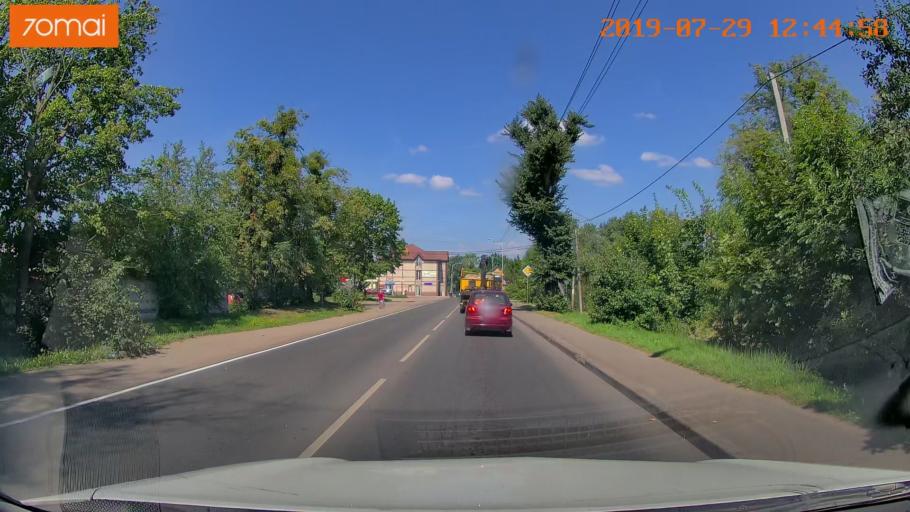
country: RU
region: Kaliningrad
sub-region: Gorod Kaliningrad
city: Kaliningrad
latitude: 54.6808
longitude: 20.5360
